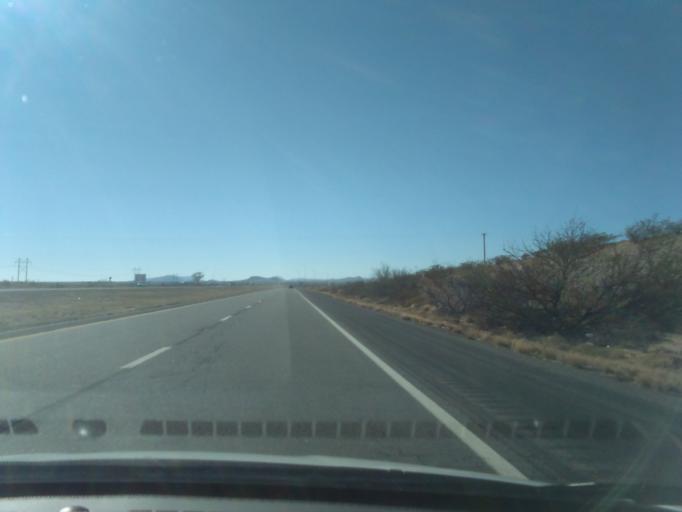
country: US
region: New Mexico
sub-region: Sierra County
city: Elephant Butte
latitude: 33.6265
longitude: -107.1331
